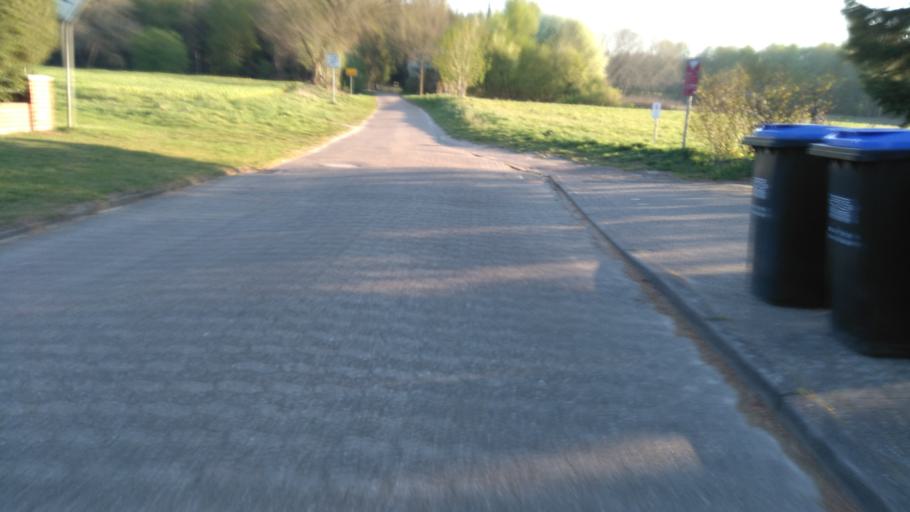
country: DE
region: Lower Saxony
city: Harsefeld
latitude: 53.4704
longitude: 9.5101
